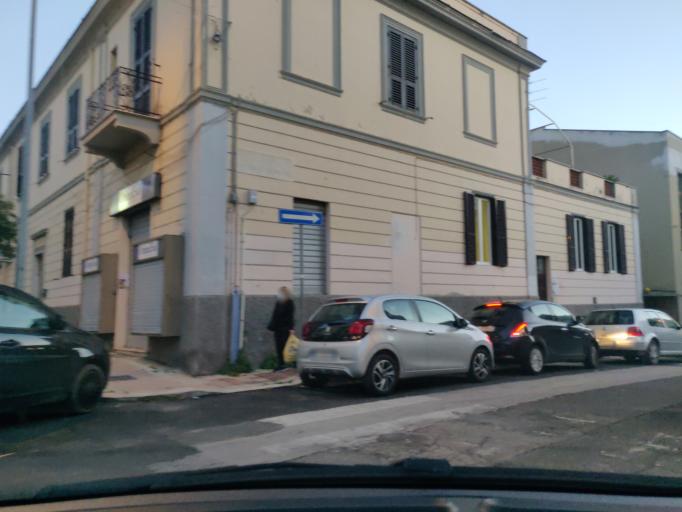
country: IT
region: Latium
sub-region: Citta metropolitana di Roma Capitale
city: Civitavecchia
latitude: 42.0903
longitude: 11.7998
